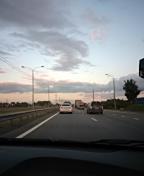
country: RU
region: Moskovskaya
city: Zhukovskiy
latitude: 55.5415
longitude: 38.0856
